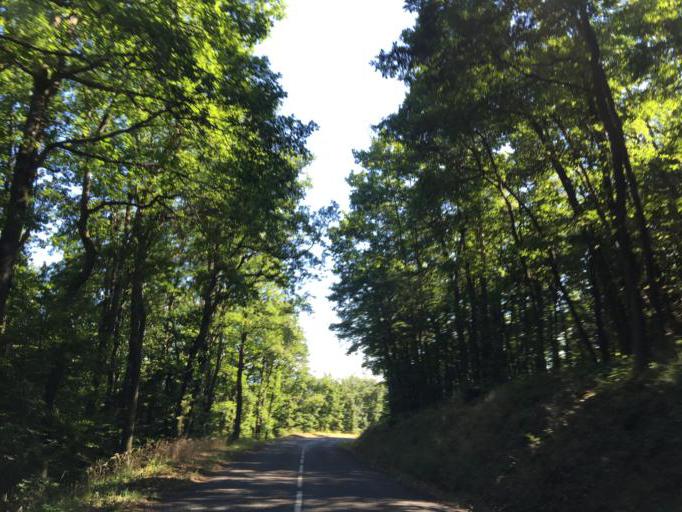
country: FR
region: Rhone-Alpes
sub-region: Departement de la Loire
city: Saint-Christo-en-Jarez
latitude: 45.5095
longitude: 4.4838
